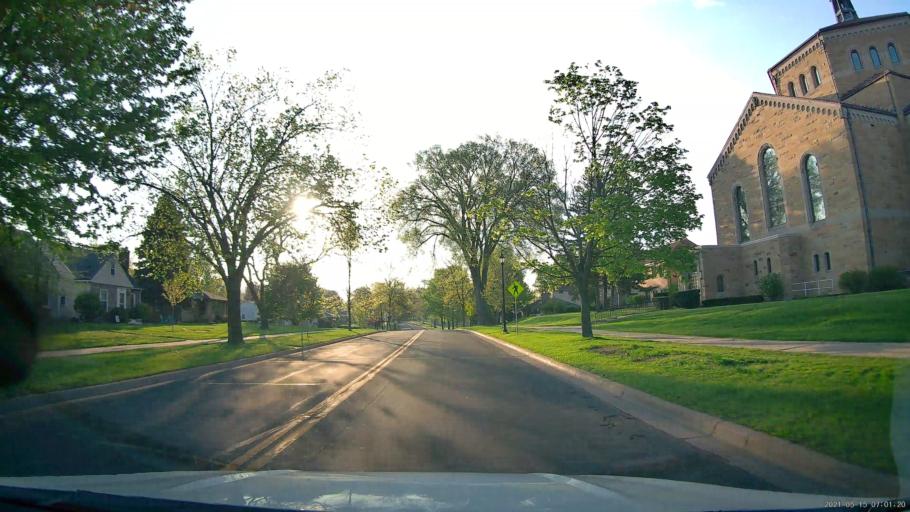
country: US
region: Minnesota
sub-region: Hennepin County
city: Saint Anthony
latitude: 45.0189
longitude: -93.2263
